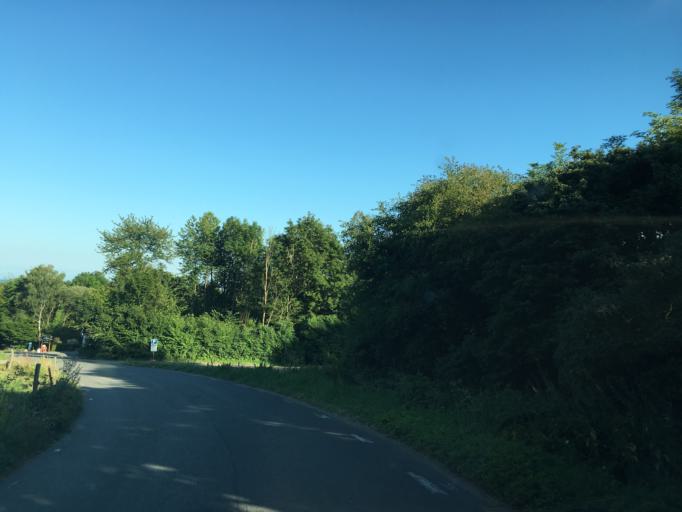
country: SE
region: Skane
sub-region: Simrishamns Kommun
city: Kivik
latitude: 55.6577
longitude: 14.2623
